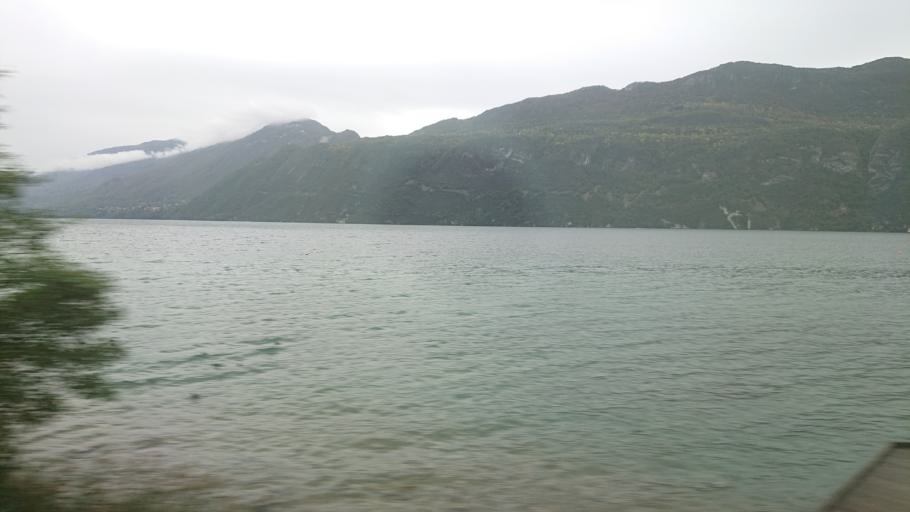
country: FR
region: Rhone-Alpes
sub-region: Departement de la Savoie
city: Brison-Saint-Innocent
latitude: 45.7193
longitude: 5.8835
